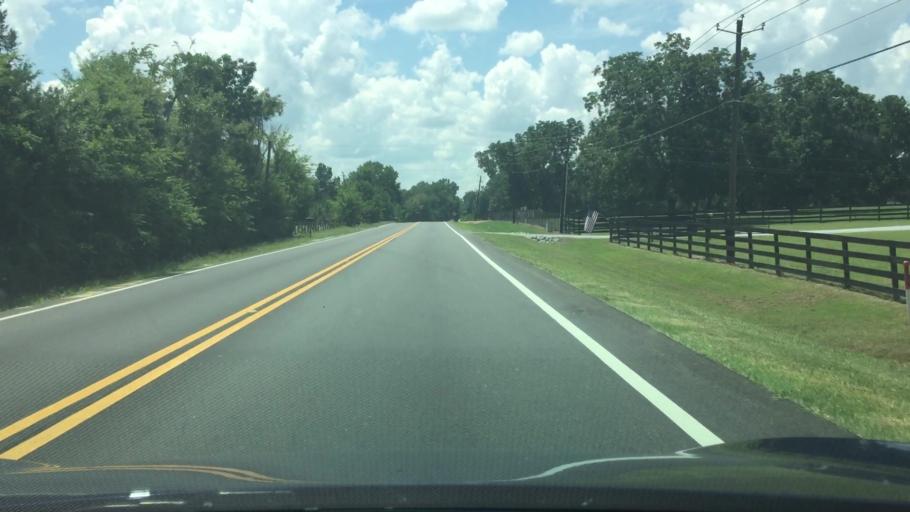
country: US
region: Alabama
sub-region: Montgomery County
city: Pike Road
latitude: 32.3229
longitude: -86.0945
